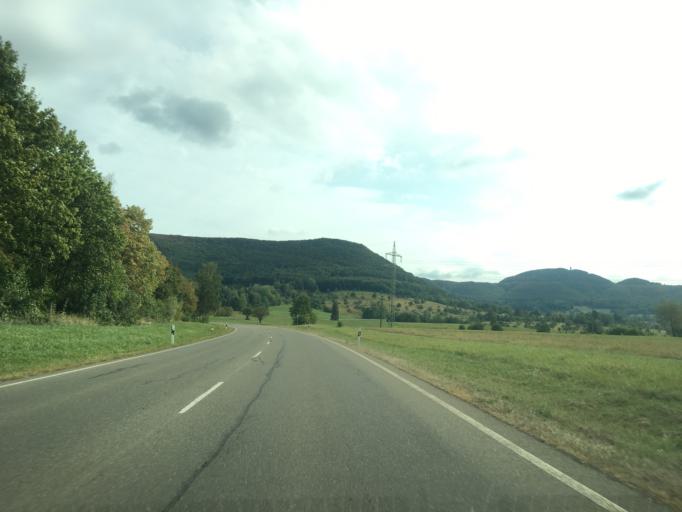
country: DE
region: Baden-Wuerttemberg
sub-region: Tuebingen Region
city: Gomaringen
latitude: 48.4532
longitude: 9.1512
